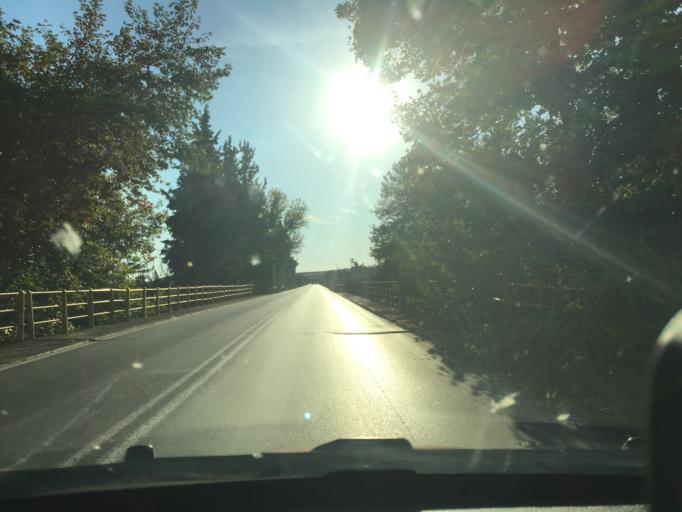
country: GR
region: Central Macedonia
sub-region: Nomos Chalkidikis
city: Olynthos
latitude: 40.2798
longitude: 23.3550
